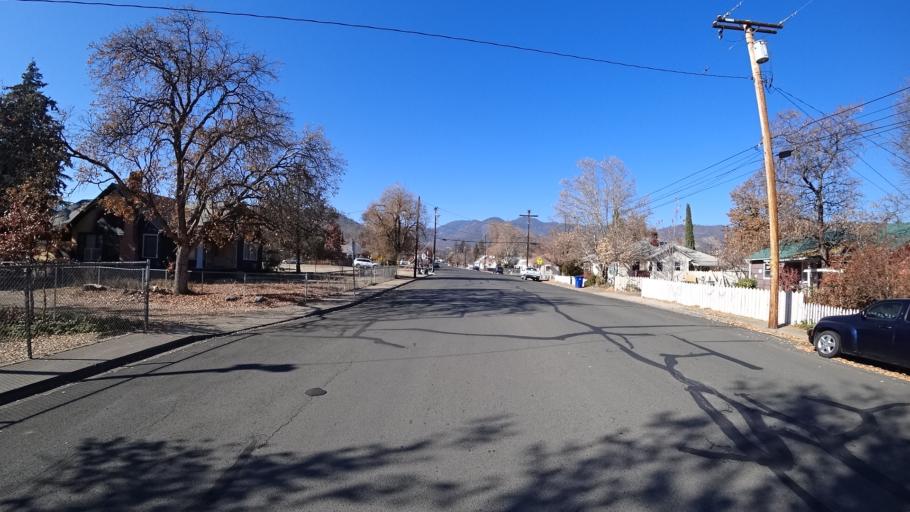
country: US
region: California
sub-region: Siskiyou County
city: Yreka
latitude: 41.7285
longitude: -122.6419
